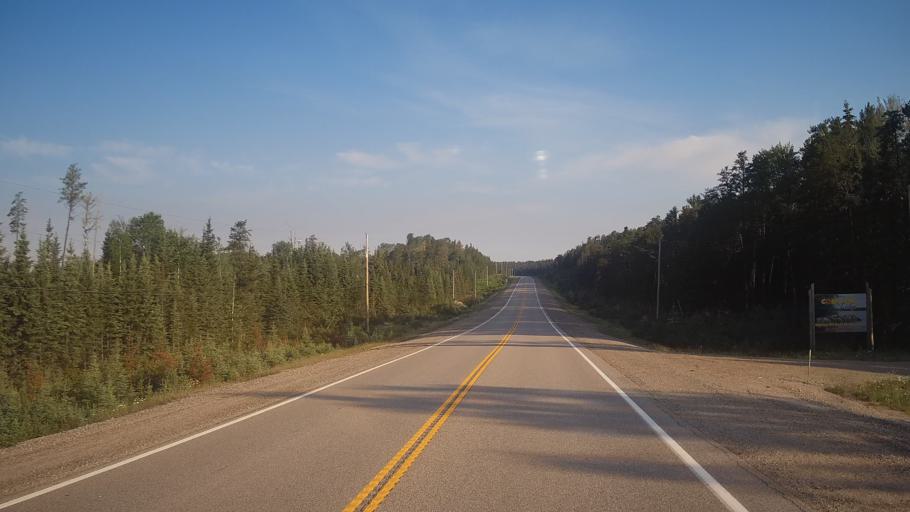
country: CA
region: Ontario
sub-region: Rainy River District
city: Atikokan
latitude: 49.3938
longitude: -91.6048
